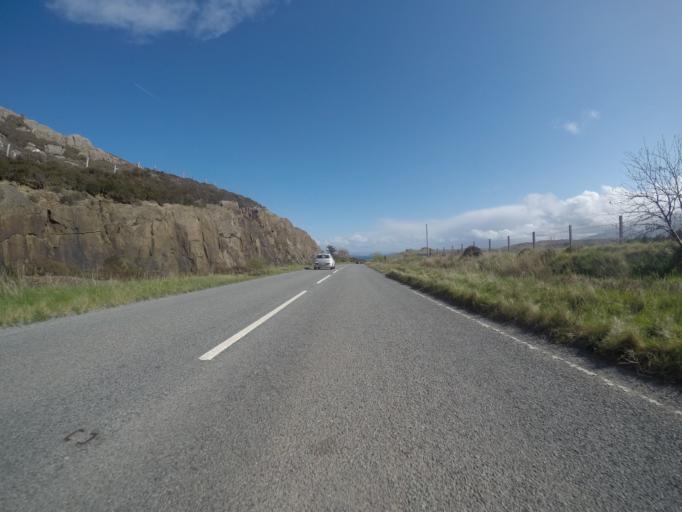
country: GB
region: Scotland
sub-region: Highland
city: Portree
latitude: 57.6133
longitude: -6.1795
